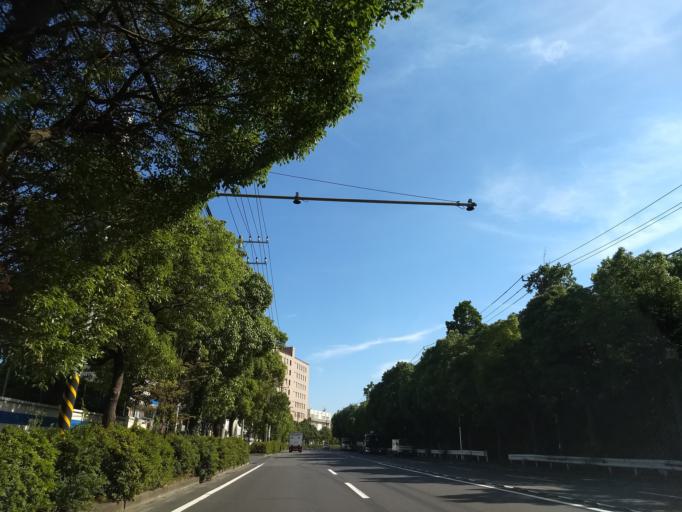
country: JP
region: Kanagawa
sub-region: Kawasaki-shi
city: Kawasaki
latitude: 35.5298
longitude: 139.7495
